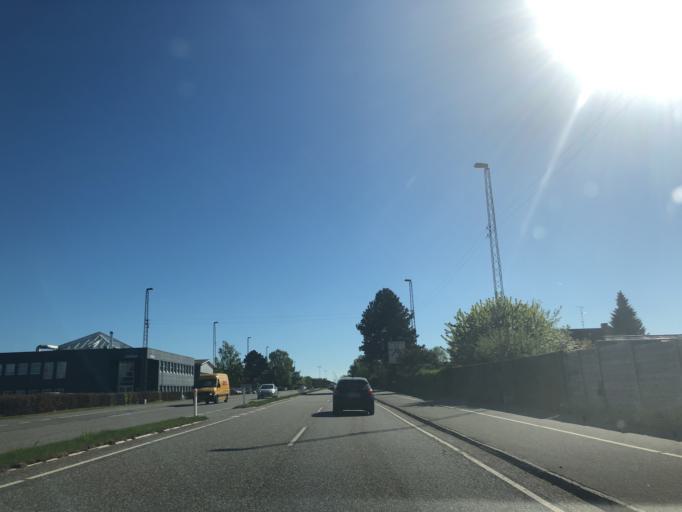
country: DK
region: Zealand
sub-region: Koge Kommune
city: Koge
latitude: 55.4447
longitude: 12.1705
